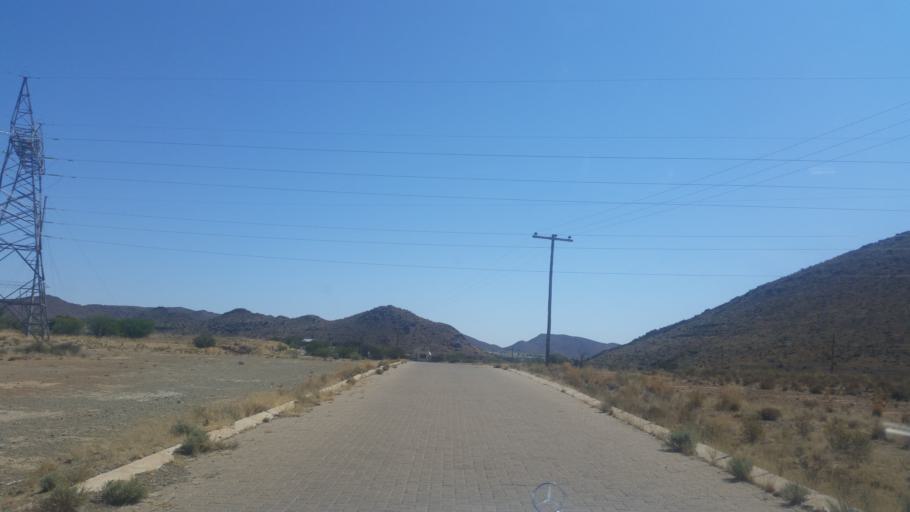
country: ZA
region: Northern Cape
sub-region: Pixley ka Seme District Municipality
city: Colesberg
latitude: -30.6241
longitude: 25.4777
